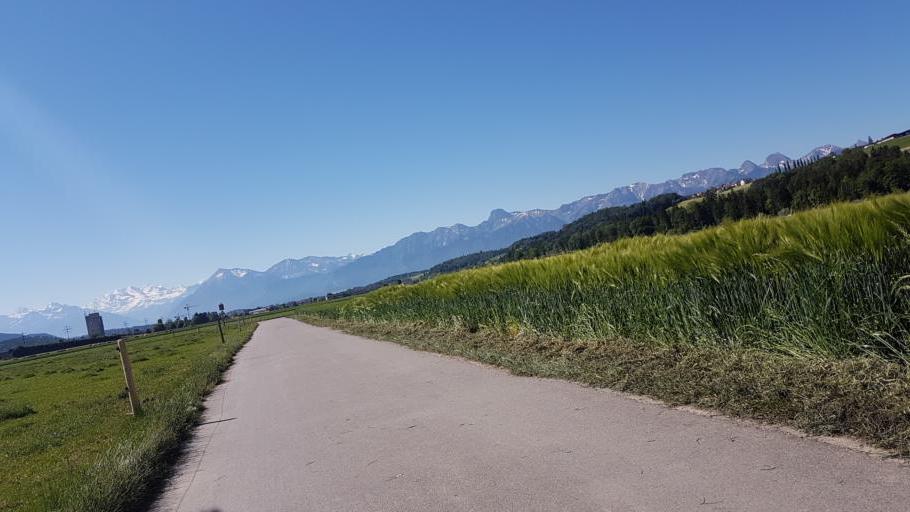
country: CH
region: Bern
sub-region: Bern-Mittelland District
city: Niederwichtrach
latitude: 46.8546
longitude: 7.5613
